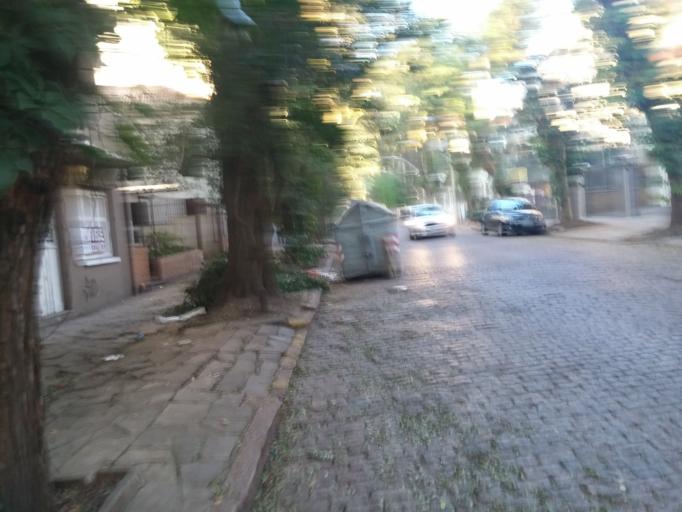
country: BR
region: Rio Grande do Sul
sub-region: Porto Alegre
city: Porto Alegre
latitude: -30.0279
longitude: -51.2138
